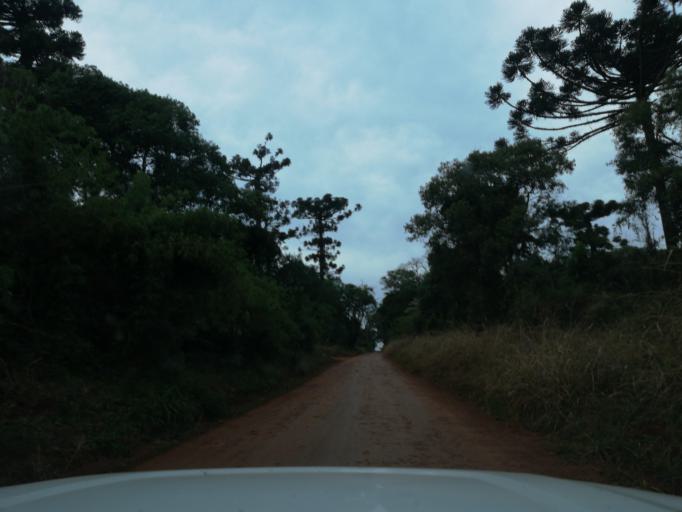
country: AR
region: Misiones
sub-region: Departamento de San Pedro
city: San Pedro
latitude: -26.6307
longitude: -54.0999
